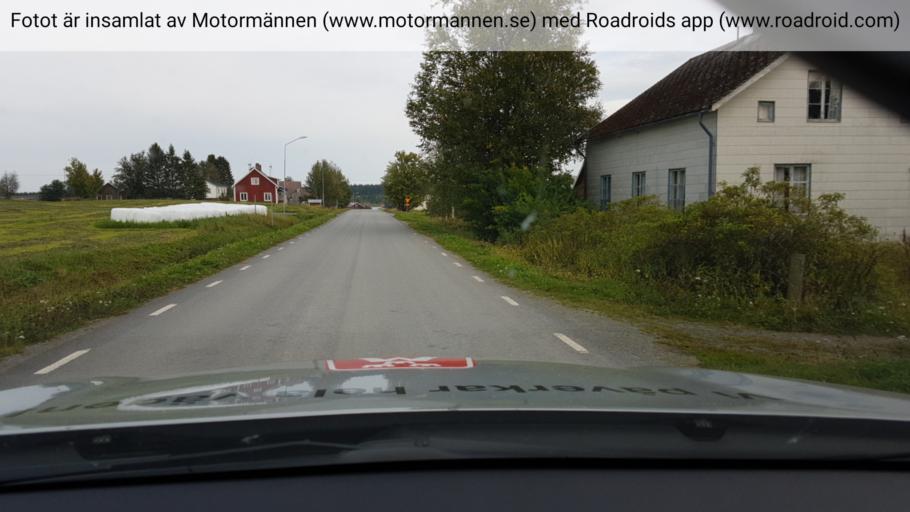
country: SE
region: Jaemtland
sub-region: OEstersunds Kommun
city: Lit
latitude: 63.6138
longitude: 14.9933
